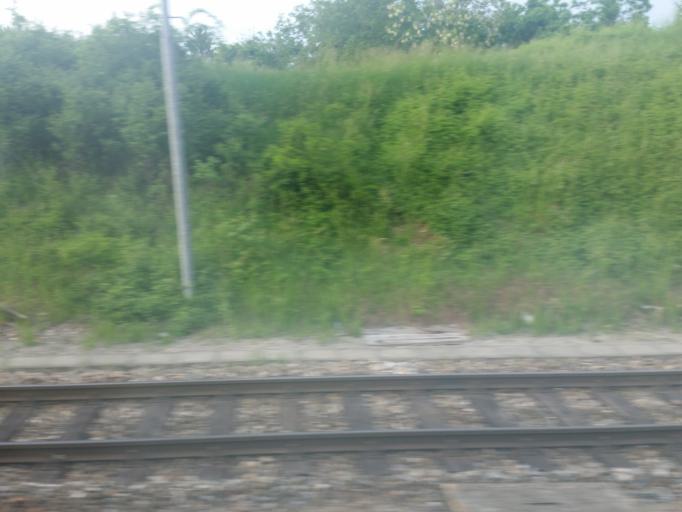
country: AT
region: Lower Austria
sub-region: Politischer Bezirk Ganserndorf
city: Marchegg
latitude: 48.2523
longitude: 16.9119
